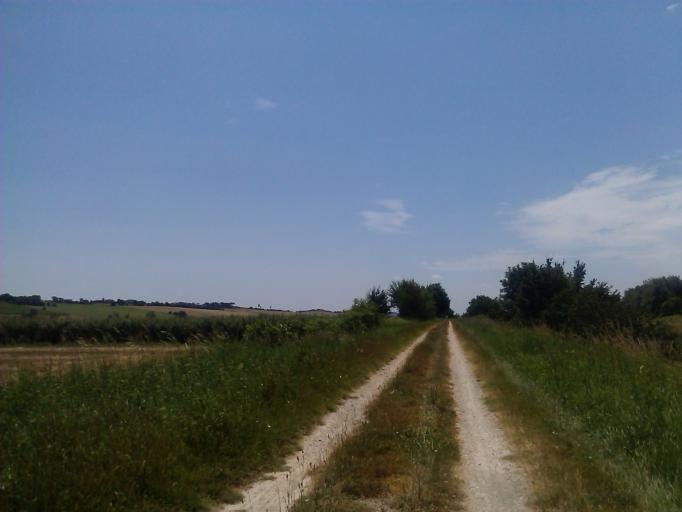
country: IT
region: Tuscany
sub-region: Province of Arezzo
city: Cesa
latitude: 43.2970
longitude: 11.8410
